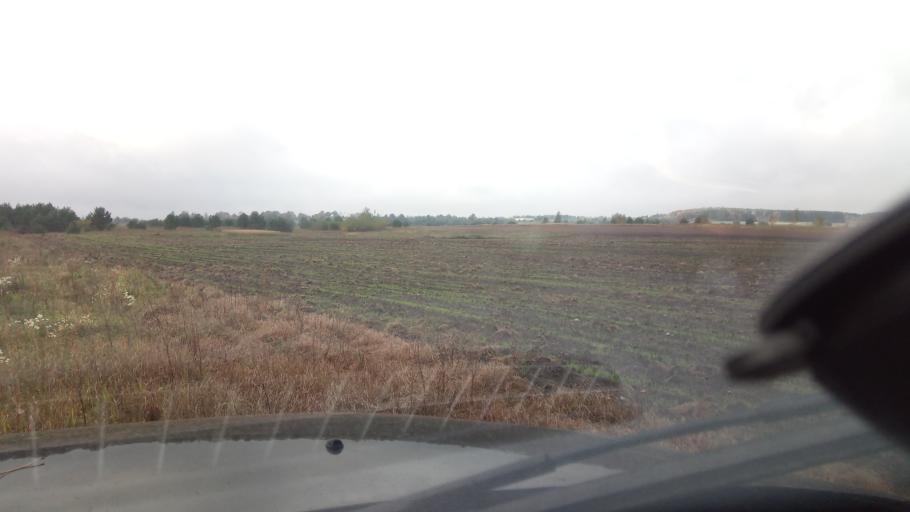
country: LT
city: Skaidiskes
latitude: 54.6241
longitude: 25.5244
